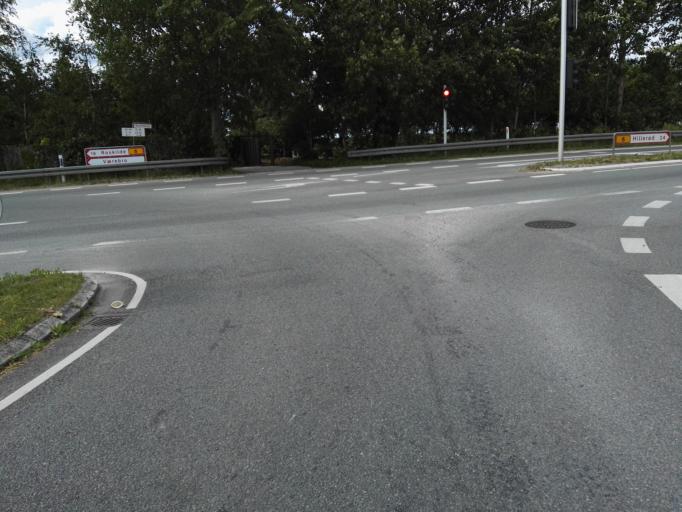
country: DK
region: Capital Region
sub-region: Egedal Kommune
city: Olstykke
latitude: 55.7694
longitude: 12.1452
